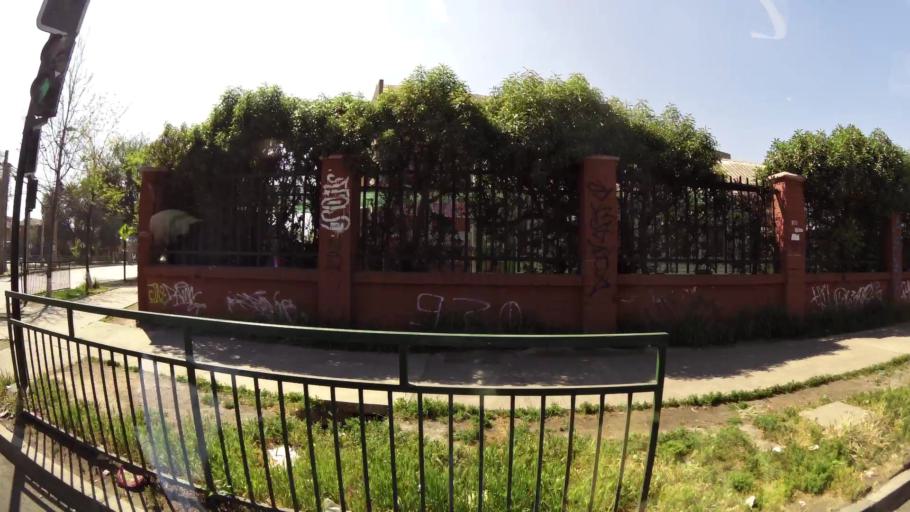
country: CL
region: Santiago Metropolitan
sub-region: Provincia de Santiago
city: Lo Prado
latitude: -33.3613
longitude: -70.7208
